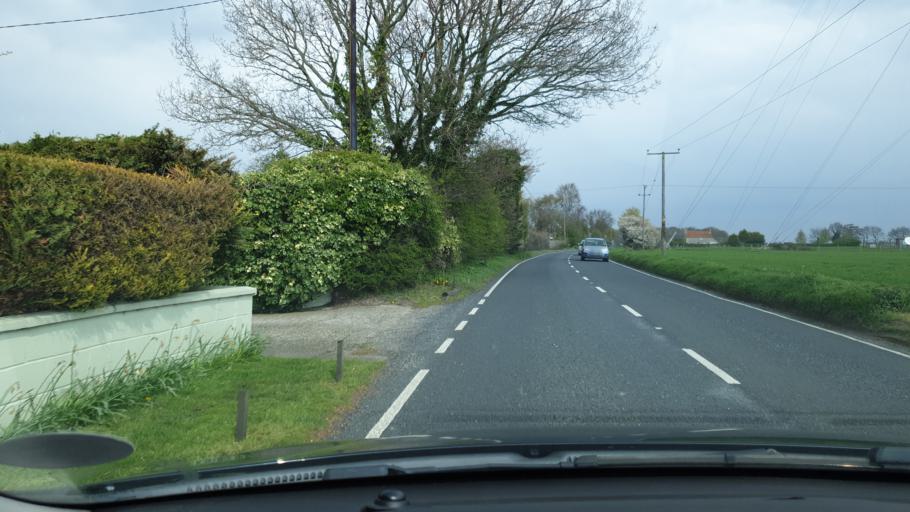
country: GB
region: England
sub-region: Essex
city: Mistley
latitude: 51.9220
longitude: 1.0847
